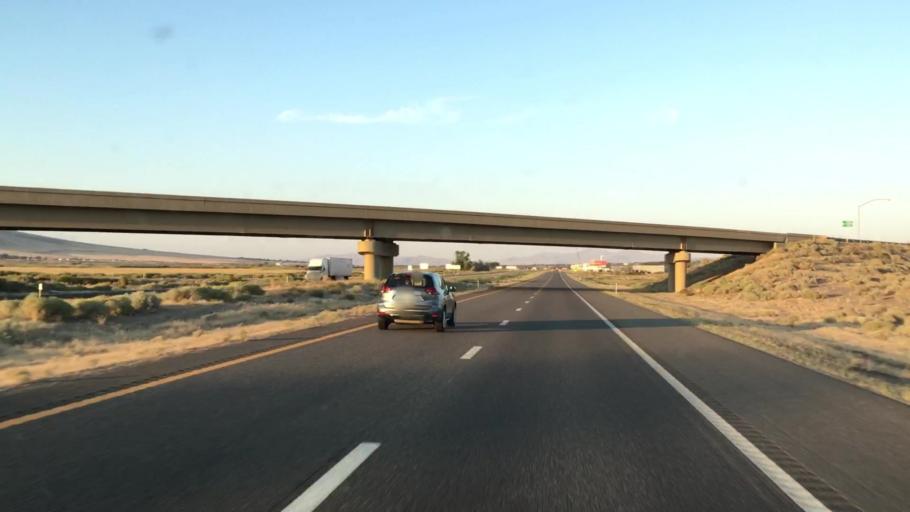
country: US
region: Nevada
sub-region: Humboldt County
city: Winnemucca
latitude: 40.9305
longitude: -117.8019
